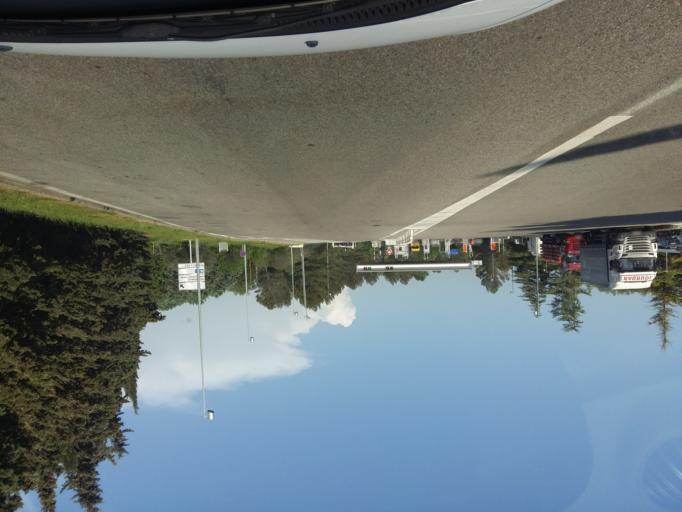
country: FR
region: Provence-Alpes-Cote d'Azur
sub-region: Departement du Var
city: Brignoles
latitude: 43.4184
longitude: 6.0639
